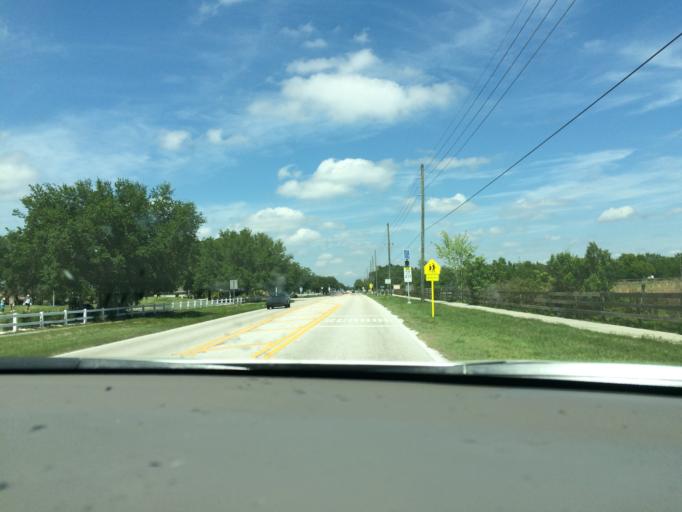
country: US
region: Florida
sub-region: Manatee County
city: Ellenton
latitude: 27.4926
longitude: -82.4337
